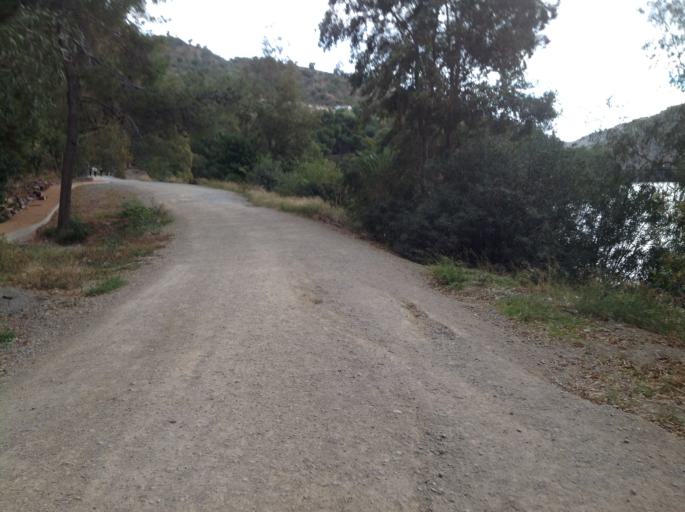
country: ES
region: Andalusia
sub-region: Provincia de Malaga
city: Carratraca
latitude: 36.9117
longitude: -4.7632
